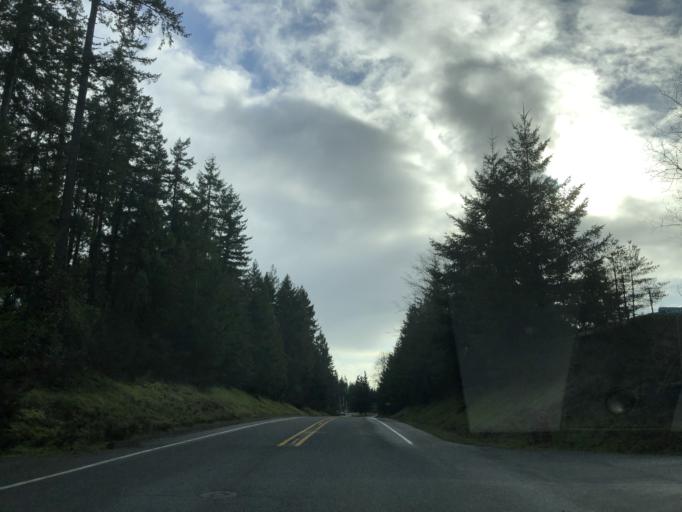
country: US
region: Washington
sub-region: Kitsap County
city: Poulsbo
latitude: 47.7680
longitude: -122.6546
